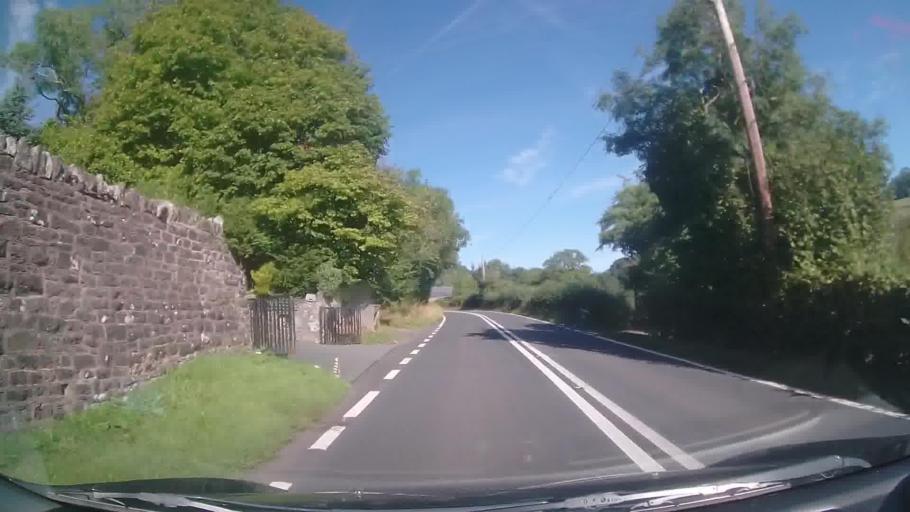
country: GB
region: Wales
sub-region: Sir Powys
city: Hay
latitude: 51.9578
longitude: -3.2027
